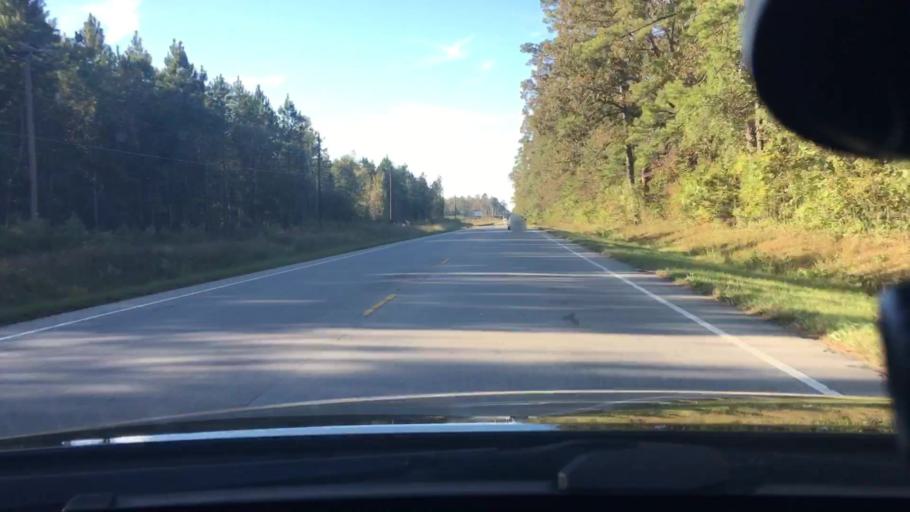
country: US
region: North Carolina
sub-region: Craven County
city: Vanceboro
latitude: 35.2446
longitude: -77.0832
